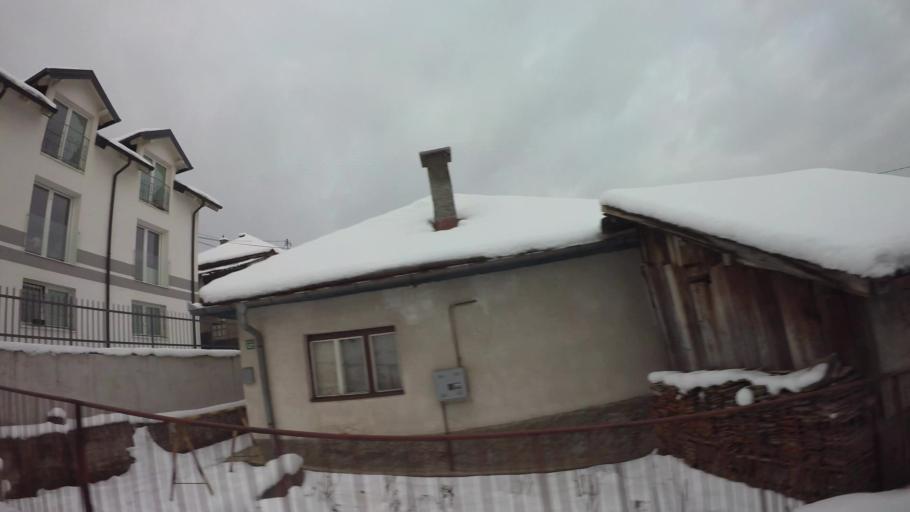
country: BA
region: Federation of Bosnia and Herzegovina
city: Kobilja Glava
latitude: 43.8612
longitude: 18.3855
